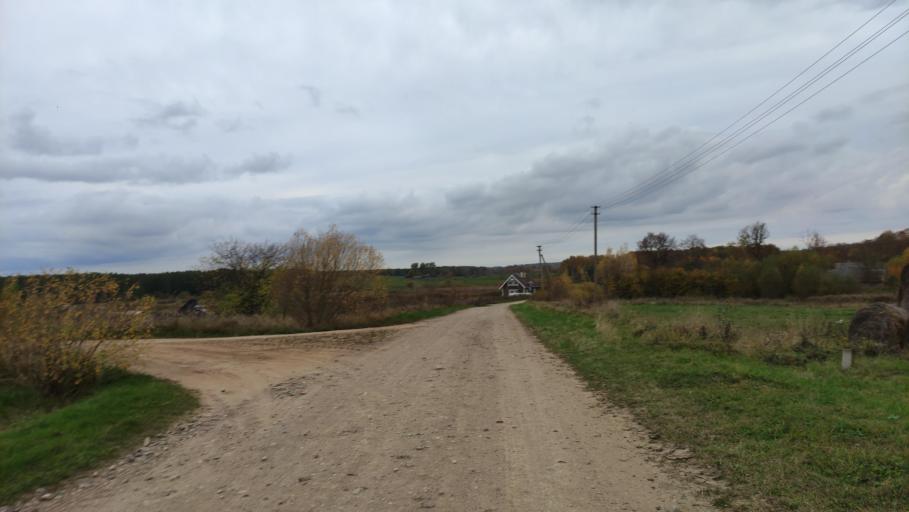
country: LT
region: Alytaus apskritis
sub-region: Alytus
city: Alytus
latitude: 54.4234
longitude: 23.8620
